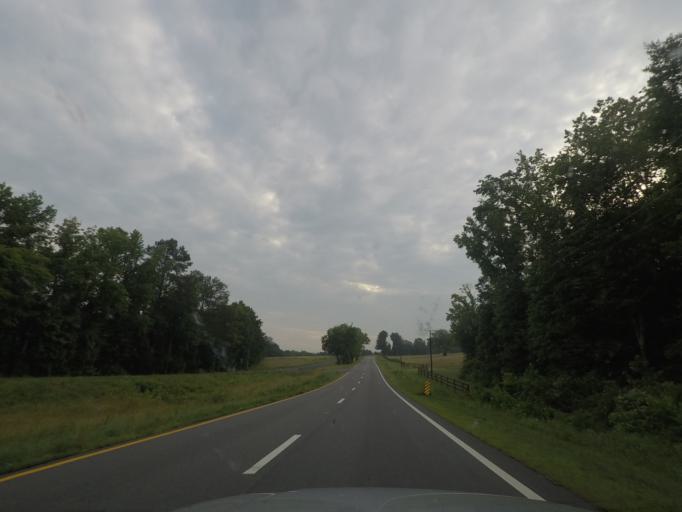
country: US
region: Virginia
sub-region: Halifax County
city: Halifax
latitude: 36.7998
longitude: -78.7756
